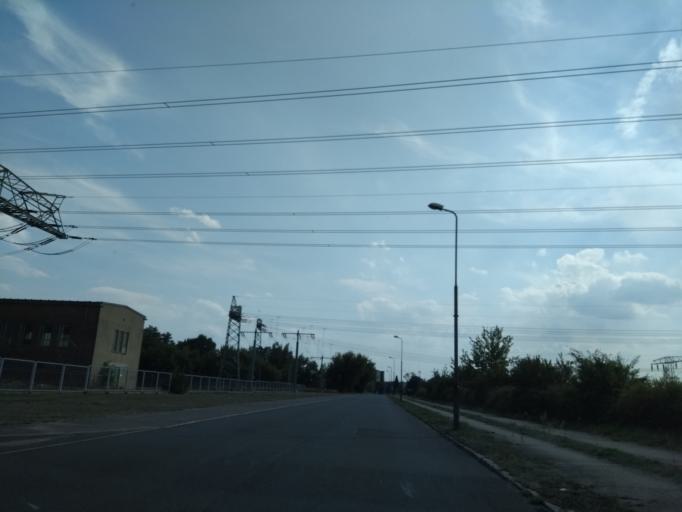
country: DE
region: Brandenburg
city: Lubbenau
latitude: 51.8488
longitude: 13.9610
